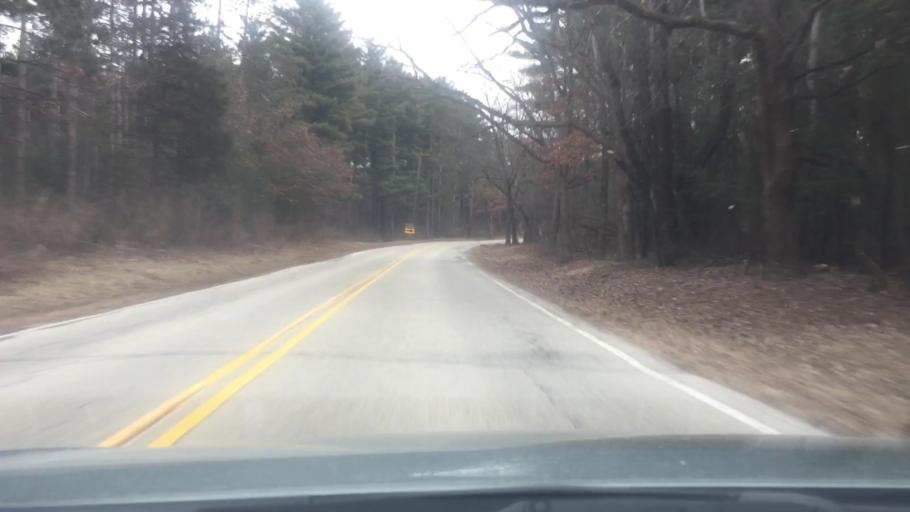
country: US
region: Wisconsin
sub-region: Waukesha County
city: North Prairie
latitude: 42.9425
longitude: -88.4442
